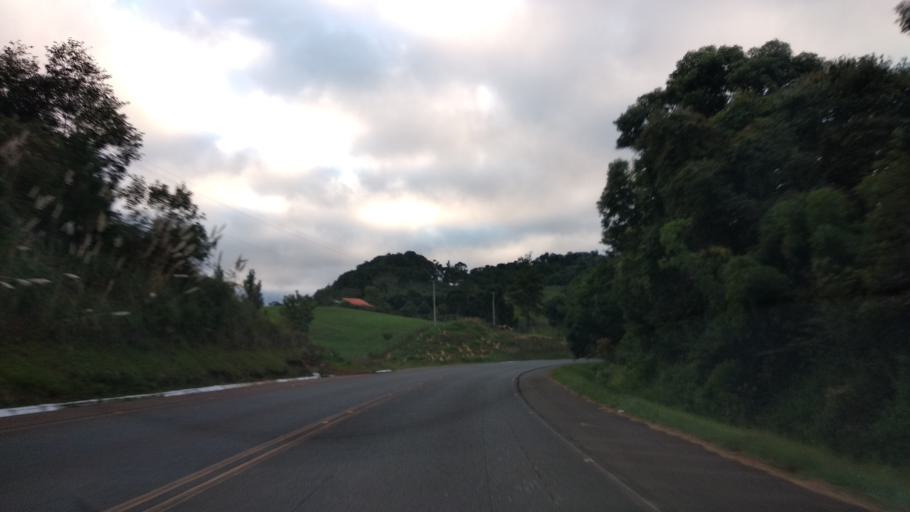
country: BR
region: Santa Catarina
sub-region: Campos Novos
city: Campos Novos
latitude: -27.4964
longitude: -50.9410
